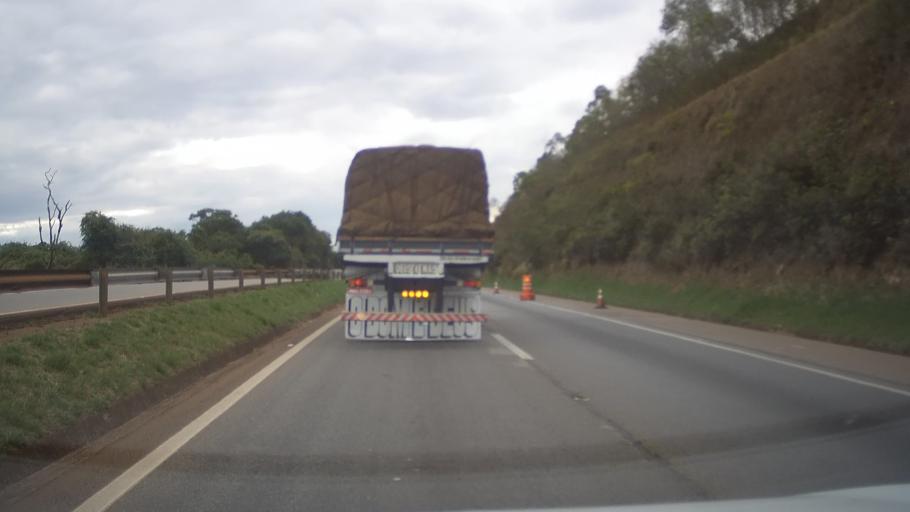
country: BR
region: Minas Gerais
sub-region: Itauna
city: Itauna
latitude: -20.3298
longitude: -44.4533
